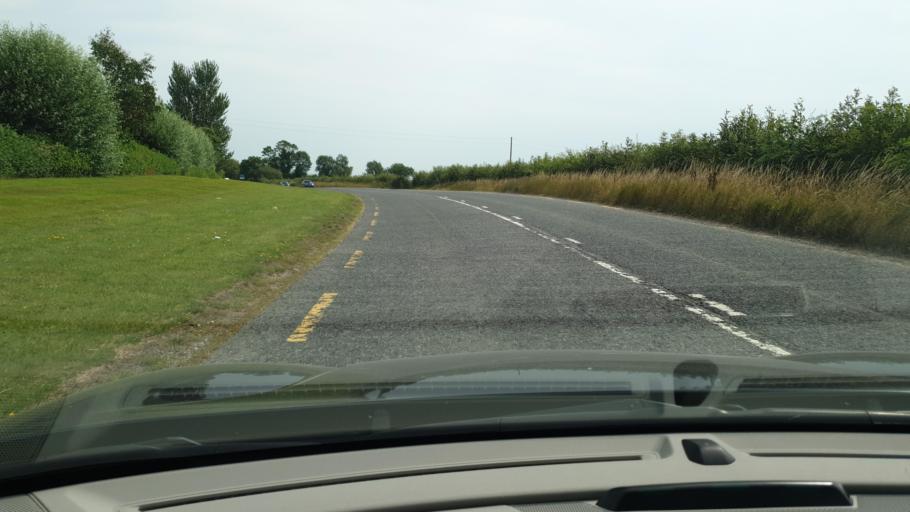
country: IE
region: Leinster
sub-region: An Mhi
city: Navan
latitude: 53.6378
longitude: -6.6084
